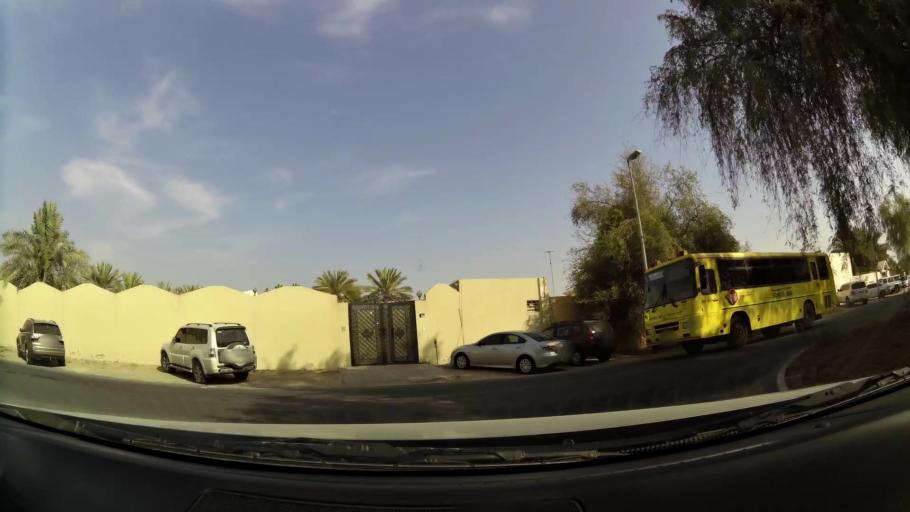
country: AE
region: Ash Shariqah
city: Sharjah
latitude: 25.2200
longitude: 55.3965
